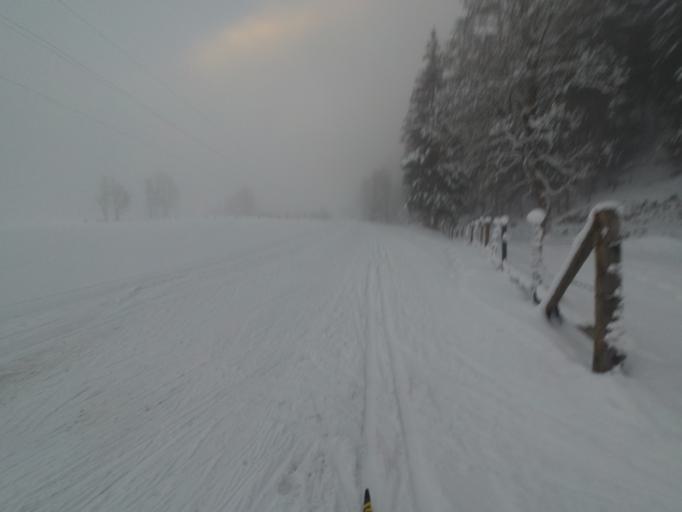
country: AT
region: Salzburg
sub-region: Politischer Bezirk Sankt Johann im Pongau
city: Wagrain
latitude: 47.3490
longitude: 13.3158
